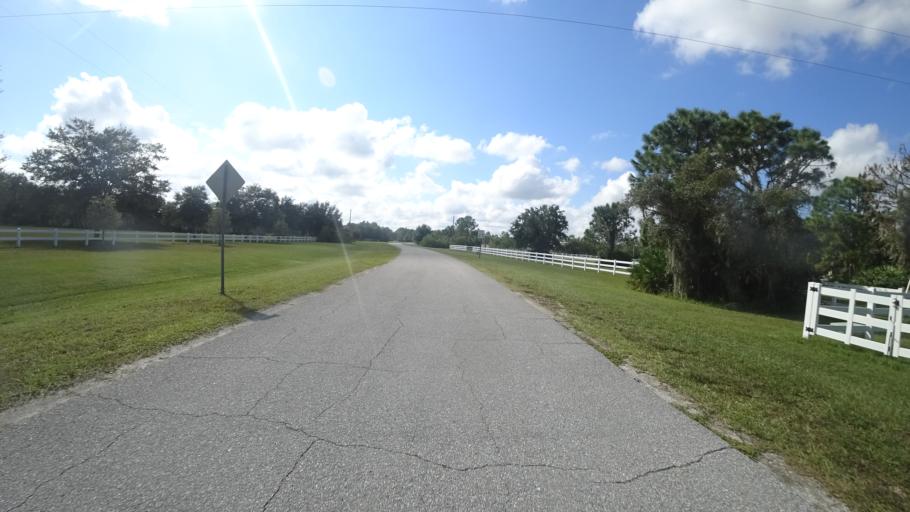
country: US
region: Florida
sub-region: Sarasota County
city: The Meadows
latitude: 27.4013
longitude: -82.3245
